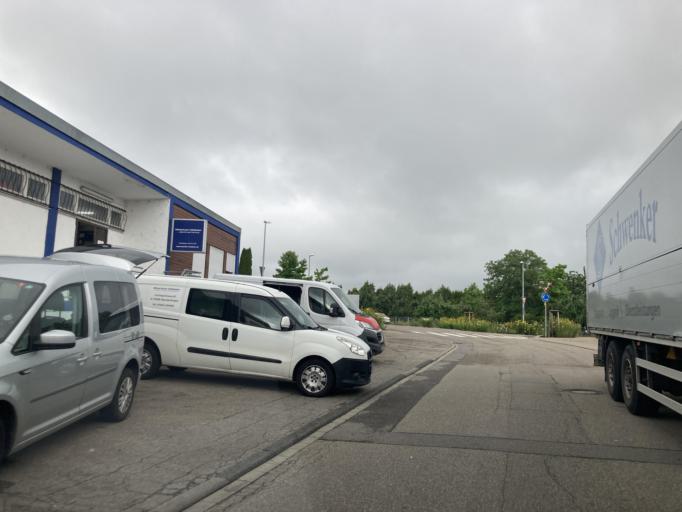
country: DE
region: Baden-Wuerttemberg
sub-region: Karlsruhe Region
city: Oberderdingen
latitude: 49.0674
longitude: 8.8070
